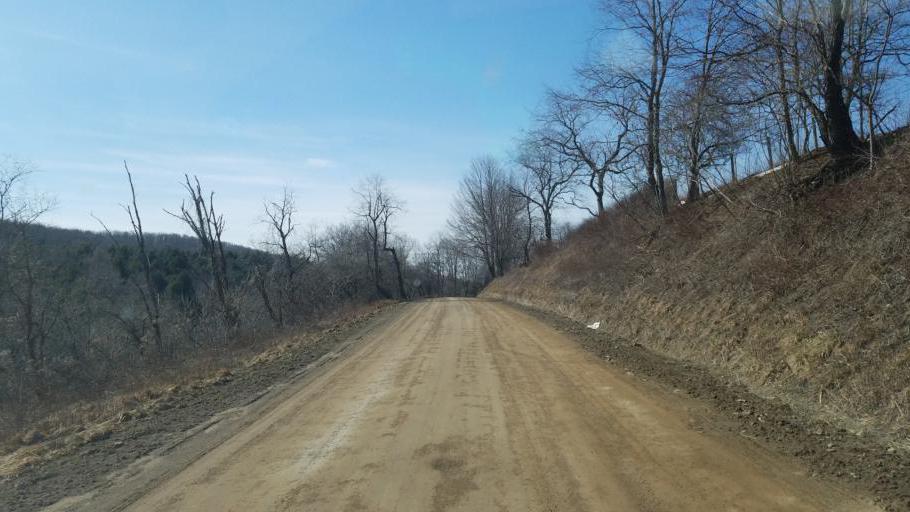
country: US
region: New York
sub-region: Allegany County
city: Andover
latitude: 41.9504
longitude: -77.7727
